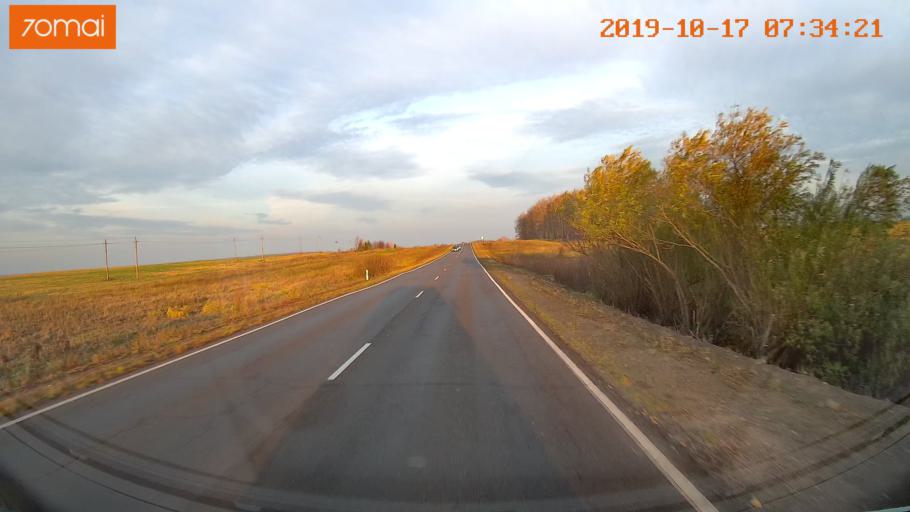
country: RU
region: Ivanovo
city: Gavrilov Posad
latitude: 56.4163
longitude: 39.9432
